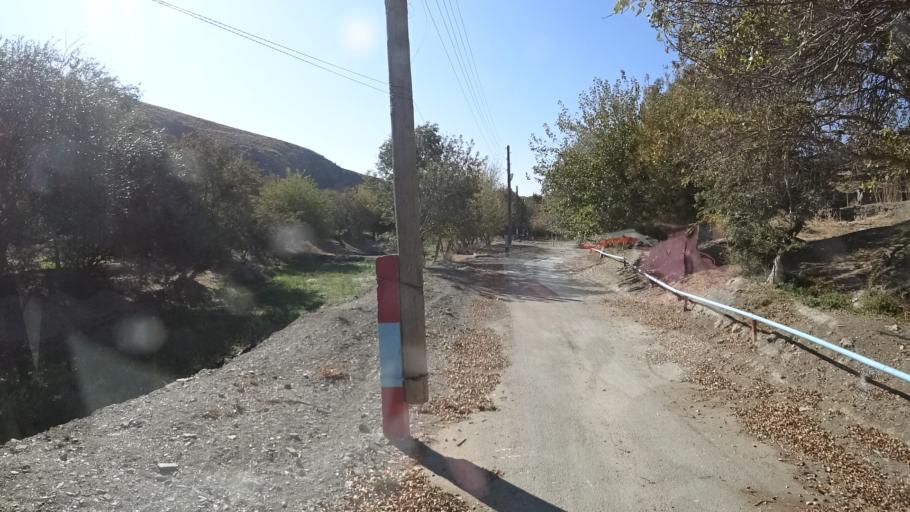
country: UZ
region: Navoiy
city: Nurota
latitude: 40.2962
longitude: 65.6052
